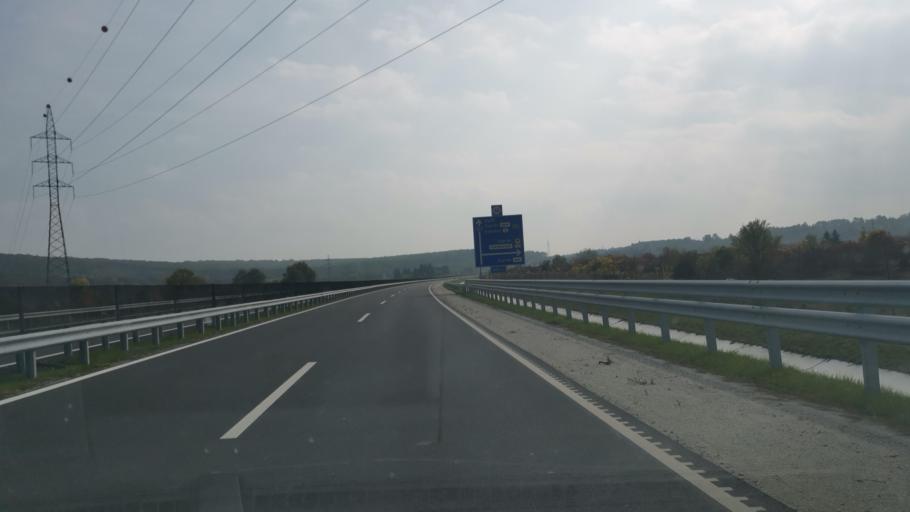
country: HU
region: Gyor-Moson-Sopron
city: Sopron
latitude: 47.6929
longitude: 16.6222
